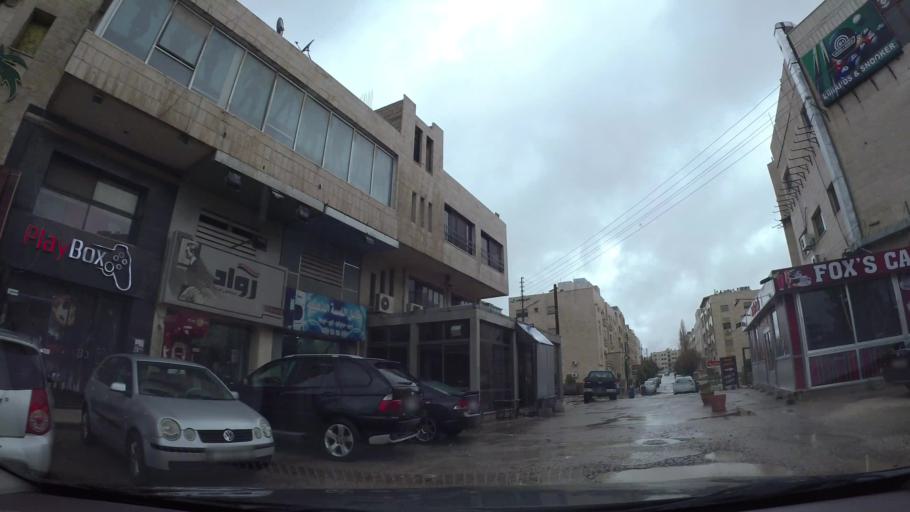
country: JO
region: Amman
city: Al Jubayhah
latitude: 32.0220
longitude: 35.8720
